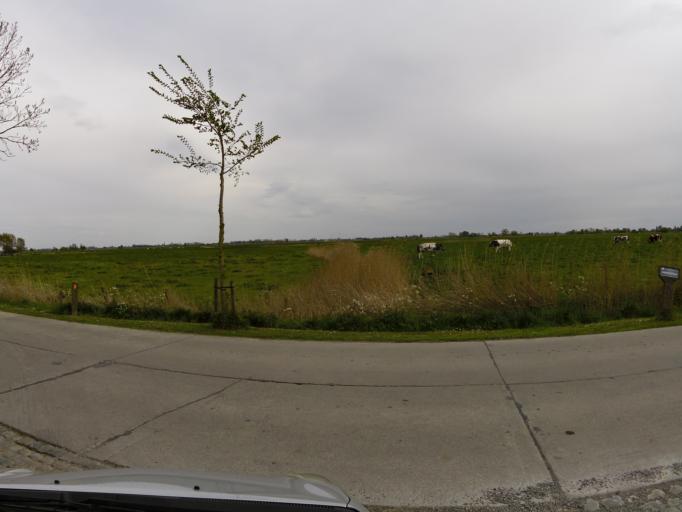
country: BE
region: Flanders
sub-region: Provincie West-Vlaanderen
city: Alveringem
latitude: 51.0326
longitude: 2.7664
